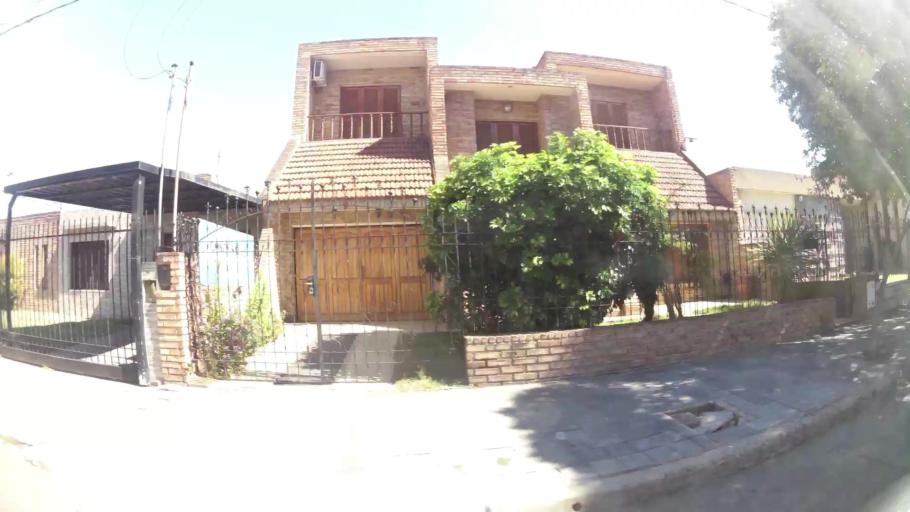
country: AR
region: Cordoba
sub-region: Departamento de Capital
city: Cordoba
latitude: -31.3779
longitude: -64.1703
